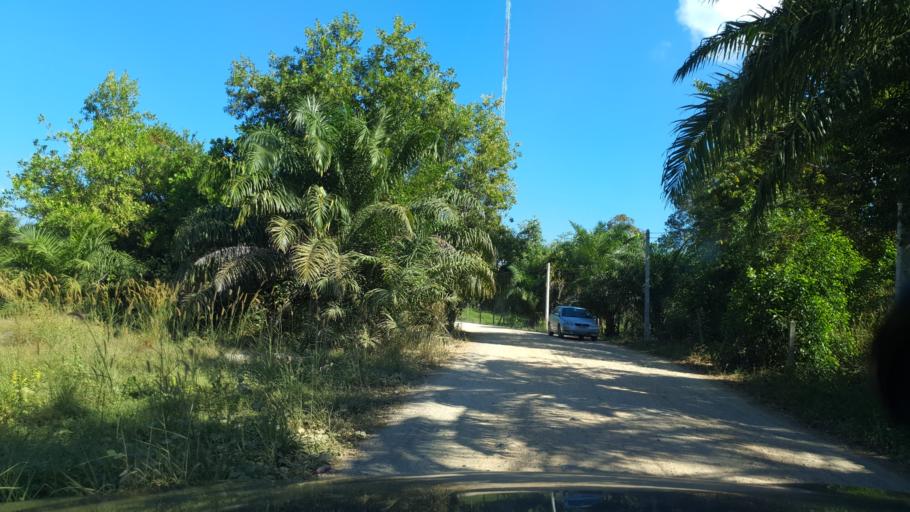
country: TH
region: Phangnga
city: Ban Ao Nang
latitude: 8.0502
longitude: 98.8019
